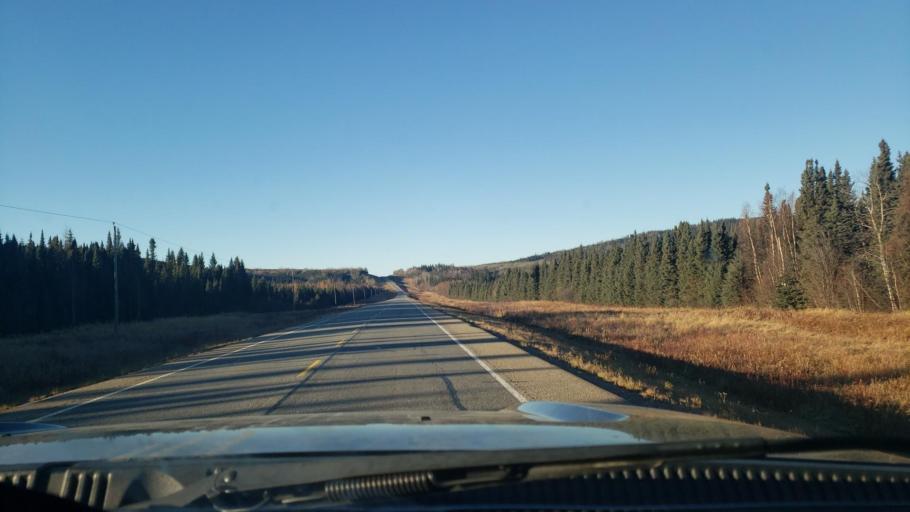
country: CA
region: British Columbia
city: Fort Nelson
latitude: 58.1645
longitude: -122.6152
